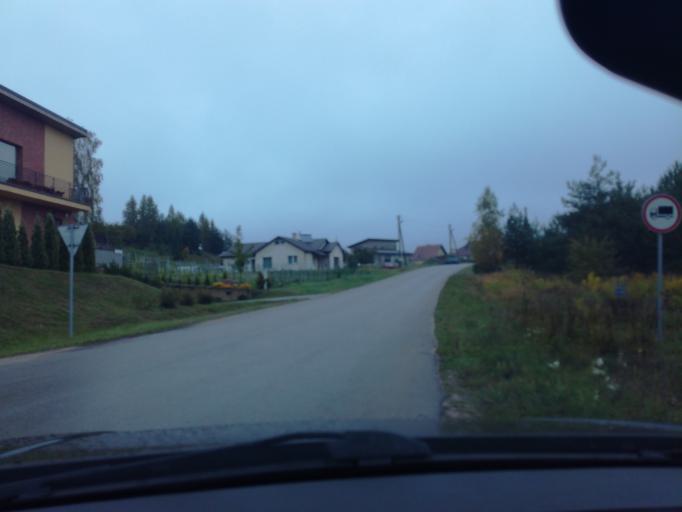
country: LT
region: Alytaus apskritis
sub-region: Alytus
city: Alytus
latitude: 54.3964
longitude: 24.0908
